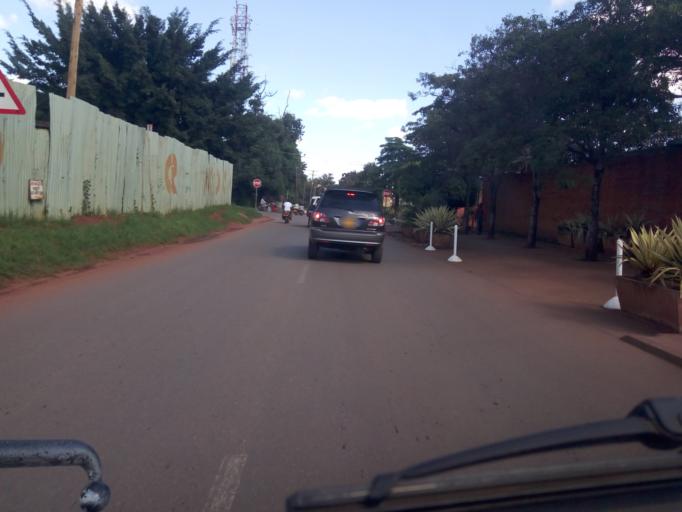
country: UG
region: Central Region
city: Kampala Central Division
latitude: 0.3202
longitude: 32.5772
